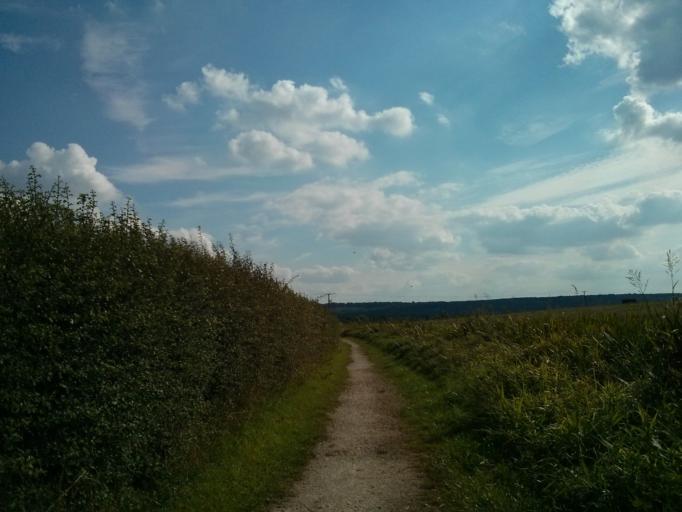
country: GB
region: England
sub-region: Lincolnshire
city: Long Bennington
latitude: 52.9128
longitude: -0.8254
